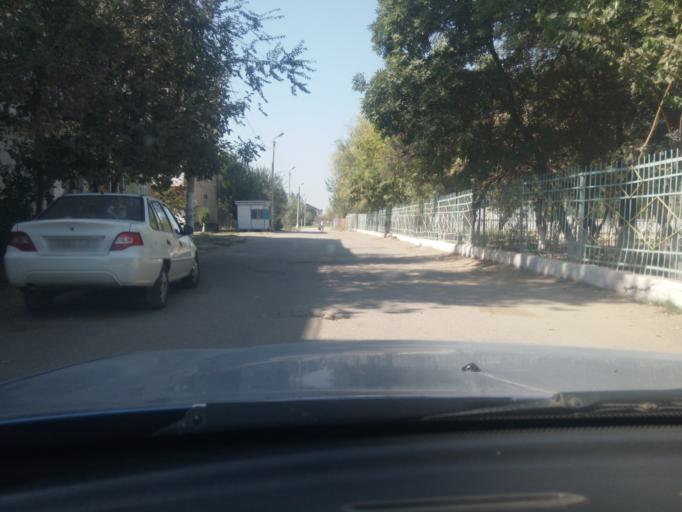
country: UZ
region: Sirdaryo
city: Guliston
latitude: 40.5157
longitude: 68.7780
